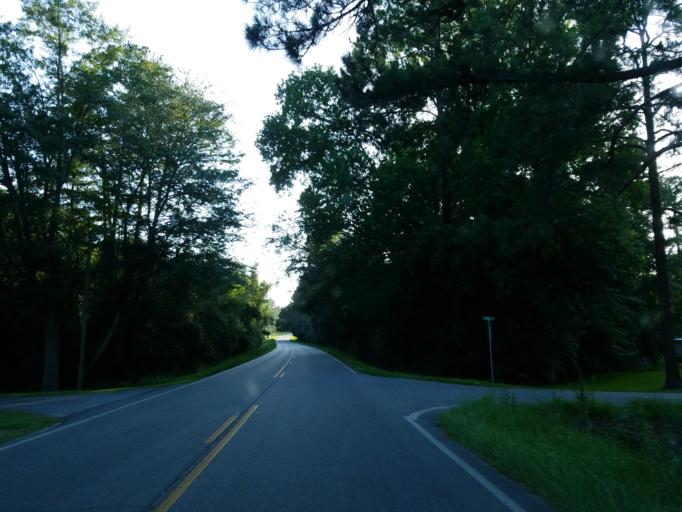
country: US
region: Georgia
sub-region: Ben Hill County
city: Fitzgerald
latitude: 31.7147
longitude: -83.2700
